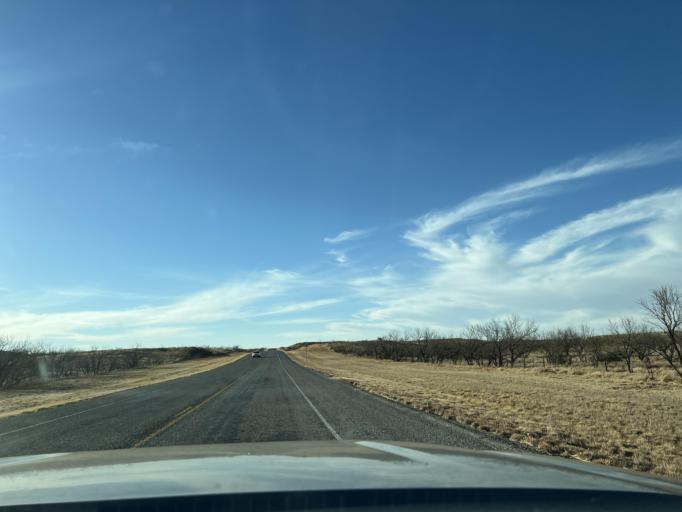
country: US
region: Texas
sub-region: Borden County
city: Gail
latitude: 32.7573
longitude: -101.2500
